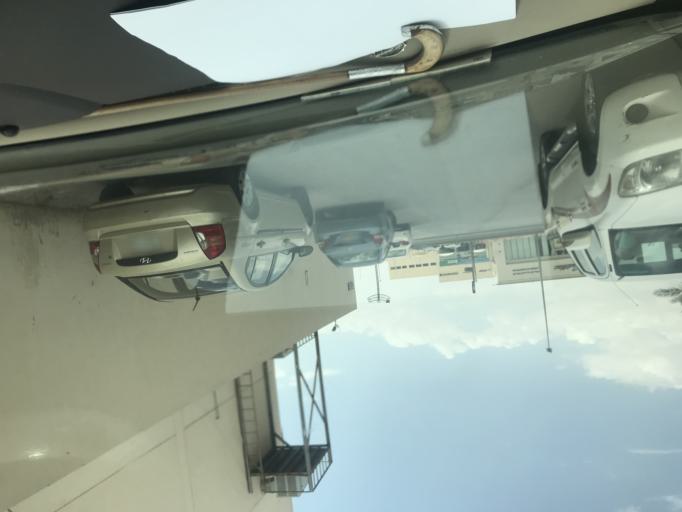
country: SA
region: Ar Riyad
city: Riyadh
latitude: 24.7284
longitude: 46.7822
